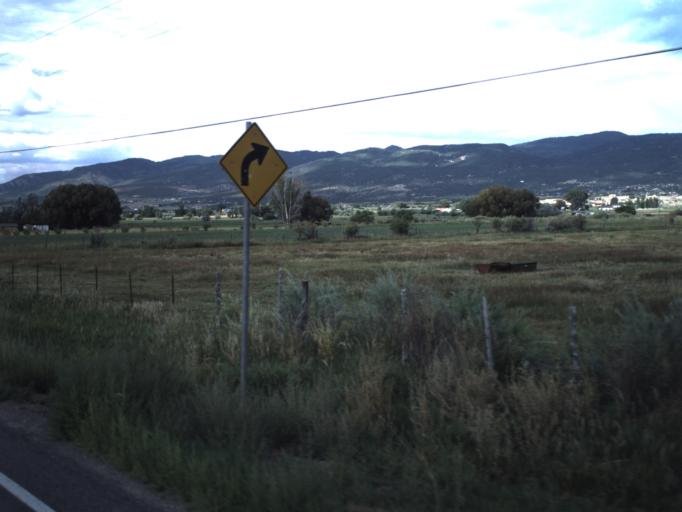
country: US
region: Utah
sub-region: Sanpete County
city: Mount Pleasant
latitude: 39.5769
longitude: -111.4554
